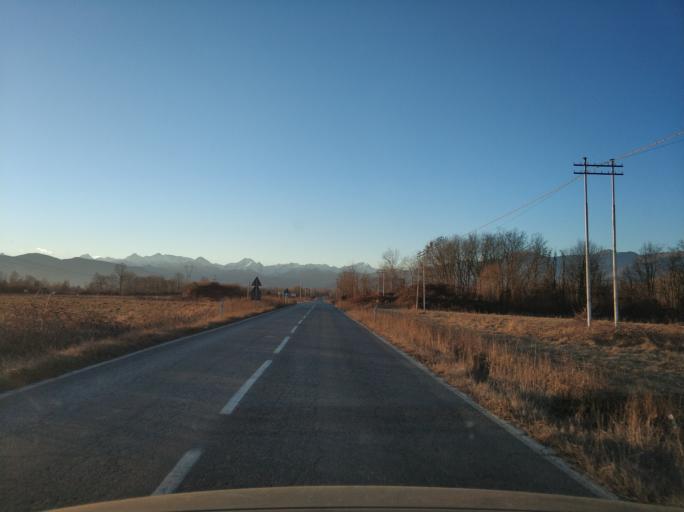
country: IT
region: Piedmont
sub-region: Provincia di Torino
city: San Francesco al Campo
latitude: 45.2502
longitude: 7.6405
